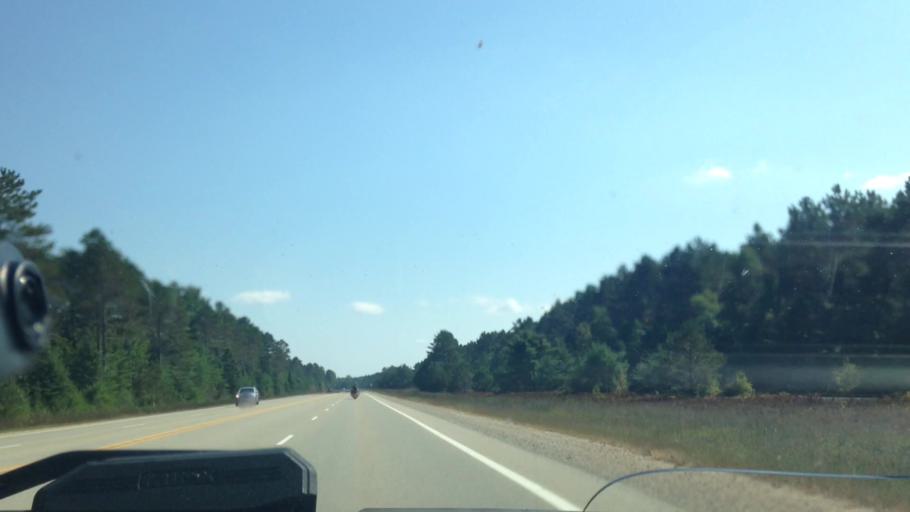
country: US
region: Michigan
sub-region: Alger County
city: Munising
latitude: 46.3568
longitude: -86.5136
